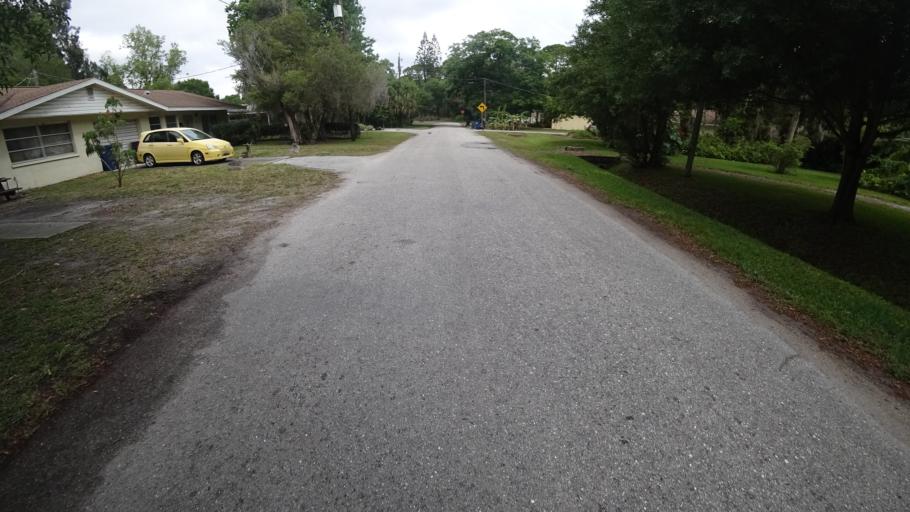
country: US
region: Florida
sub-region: Manatee County
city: South Bradenton
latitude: 27.4492
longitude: -82.5842
